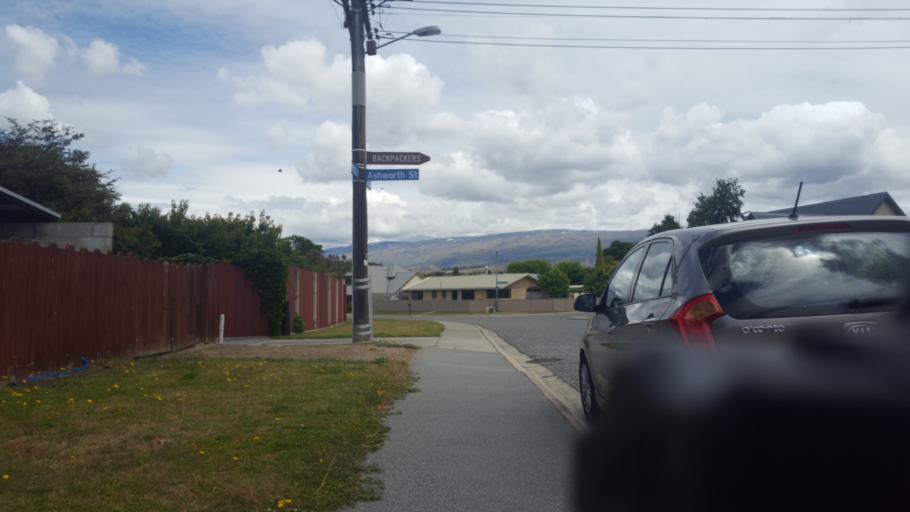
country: NZ
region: Otago
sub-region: Queenstown-Lakes District
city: Wanaka
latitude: -45.2513
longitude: 169.3837
